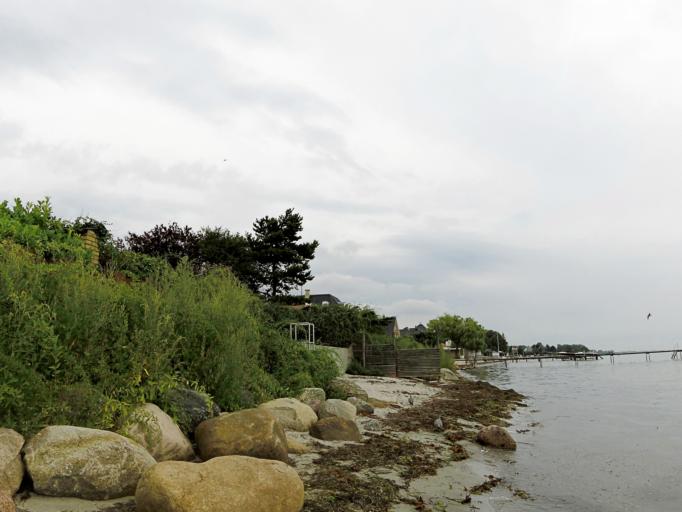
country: DK
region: Capital Region
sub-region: Gentofte Kommune
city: Charlottenlund
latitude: 55.7350
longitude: 12.5826
